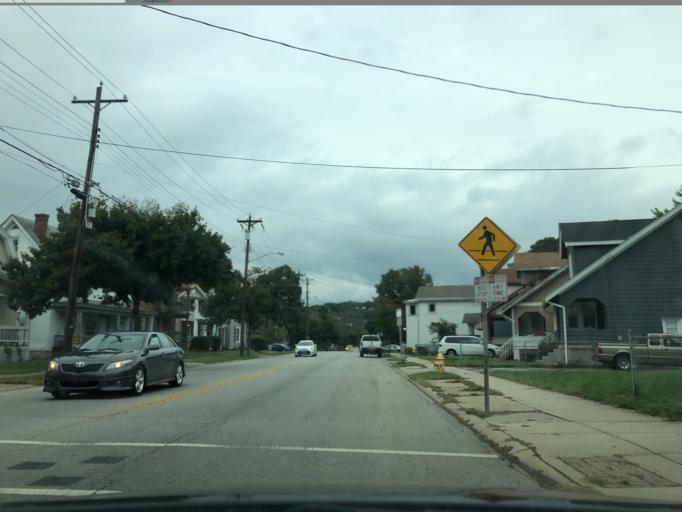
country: US
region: Ohio
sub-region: Hamilton County
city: Mariemont
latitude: 39.1539
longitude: -84.3804
